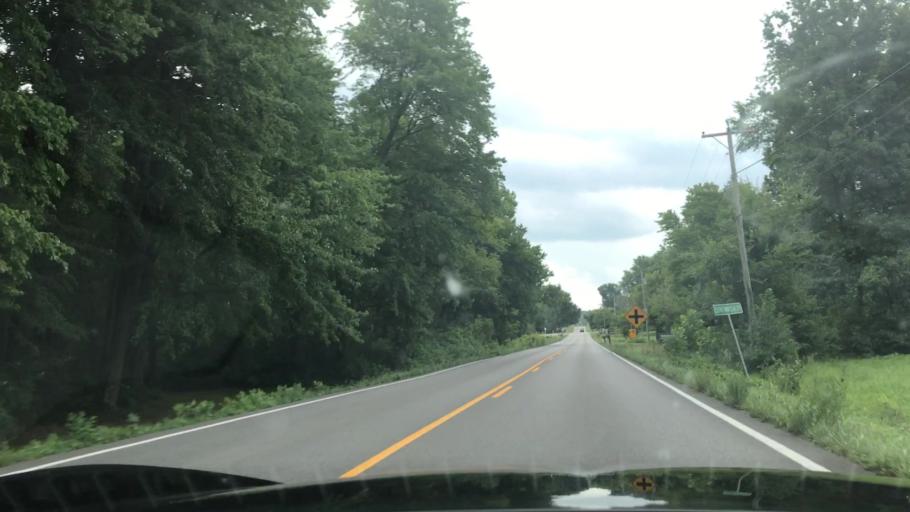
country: US
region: Kentucky
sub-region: Muhlenberg County
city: Central City
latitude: 37.2005
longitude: -87.0369
